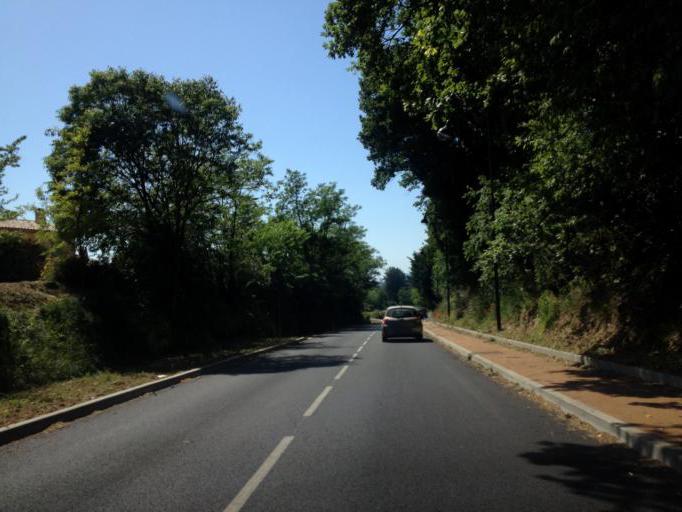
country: FR
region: Provence-Alpes-Cote d'Azur
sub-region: Departement du Vaucluse
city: Cadenet
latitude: 43.7365
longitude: 5.3630
